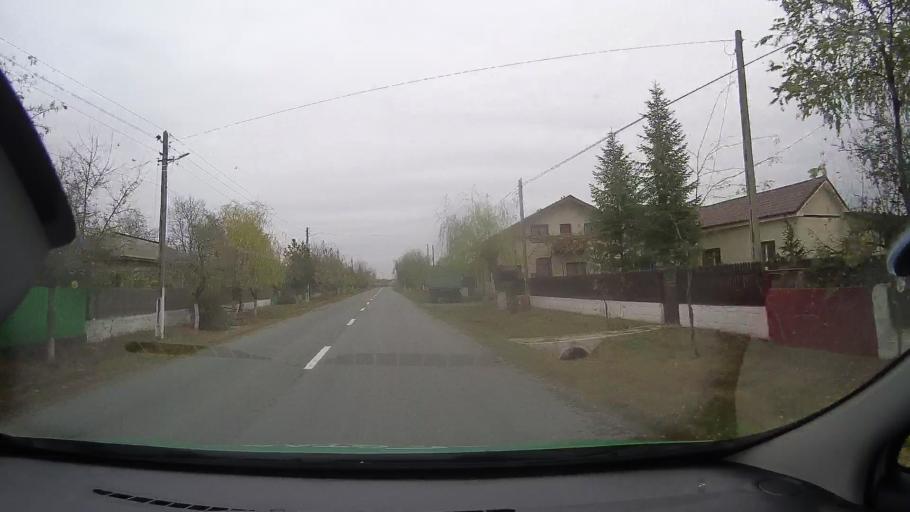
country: RO
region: Constanta
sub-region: Comuna Crucea
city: Crucea
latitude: 44.4488
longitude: 28.2411
